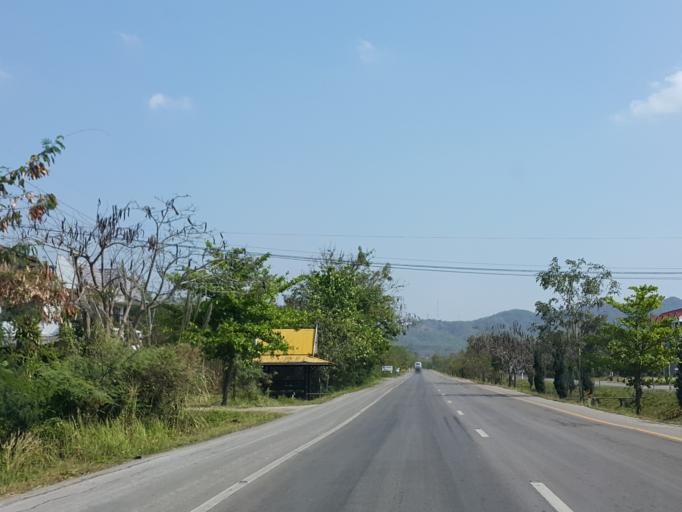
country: TH
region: Lampang
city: Lampang
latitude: 18.2704
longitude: 99.5271
